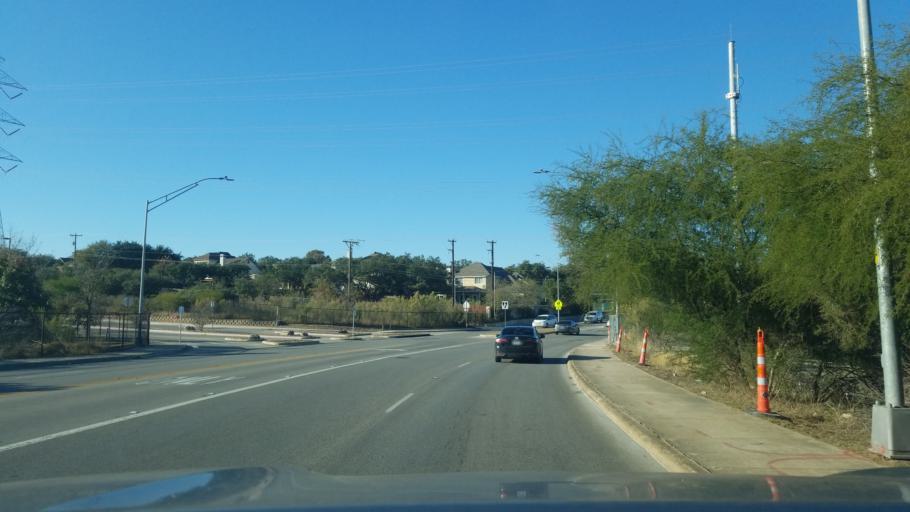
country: US
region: Texas
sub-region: Bexar County
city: Hollywood Park
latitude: 29.6308
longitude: -98.4808
